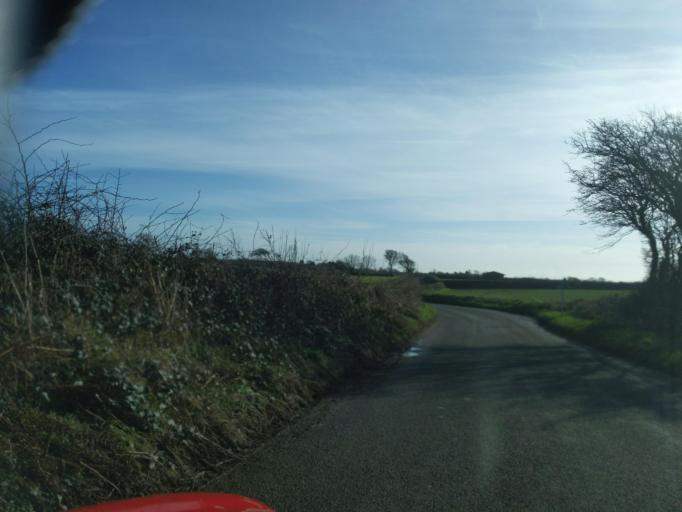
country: GB
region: England
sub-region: Devon
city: Kingsbridge
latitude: 50.3374
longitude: -3.7215
